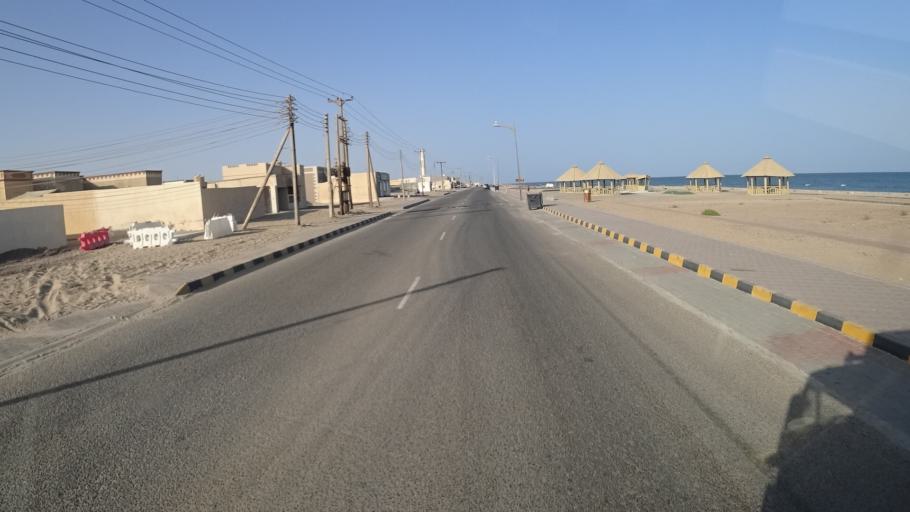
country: OM
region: Ash Sharqiyah
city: Sur
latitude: 22.1258
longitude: 59.7221
